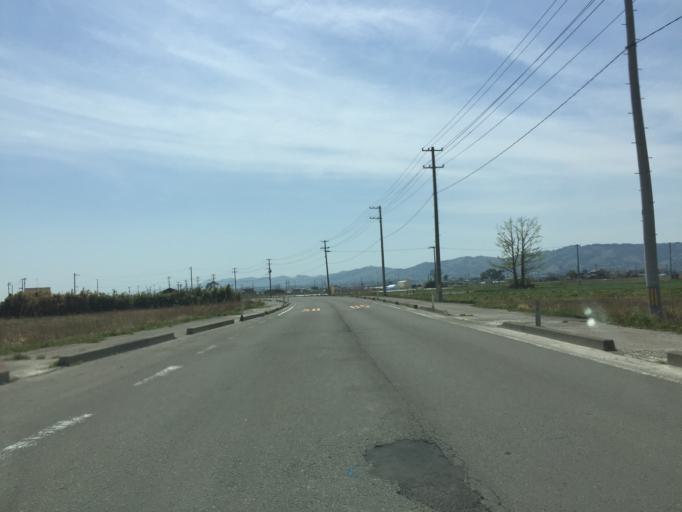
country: JP
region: Miyagi
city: Watari
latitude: 37.9933
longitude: 140.9014
